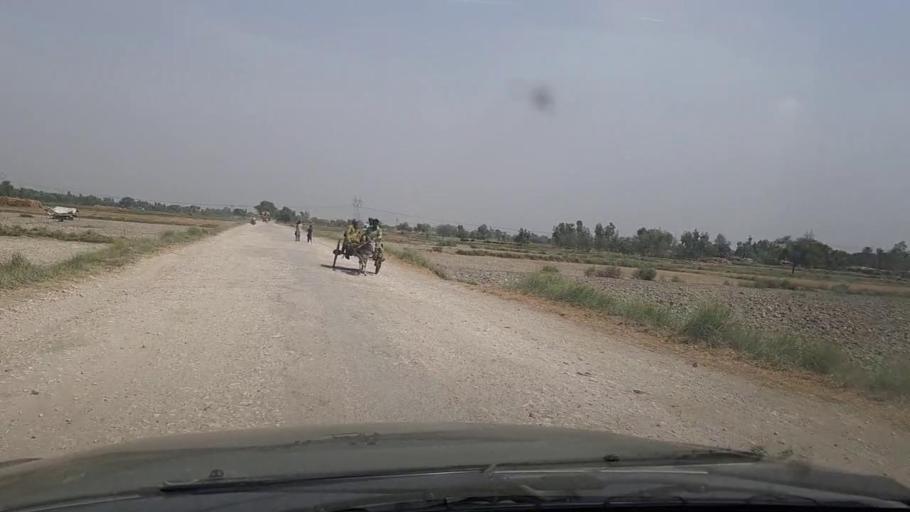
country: PK
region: Sindh
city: Shikarpur
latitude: 27.9230
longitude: 68.6724
